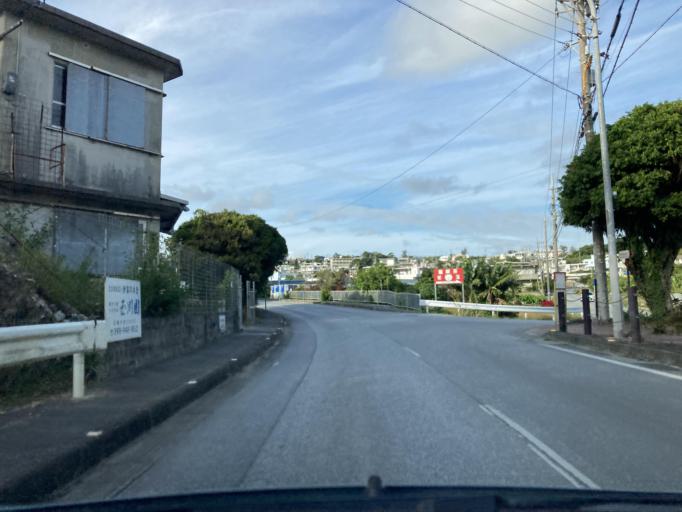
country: JP
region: Okinawa
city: Tomigusuku
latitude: 26.1419
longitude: 127.7478
